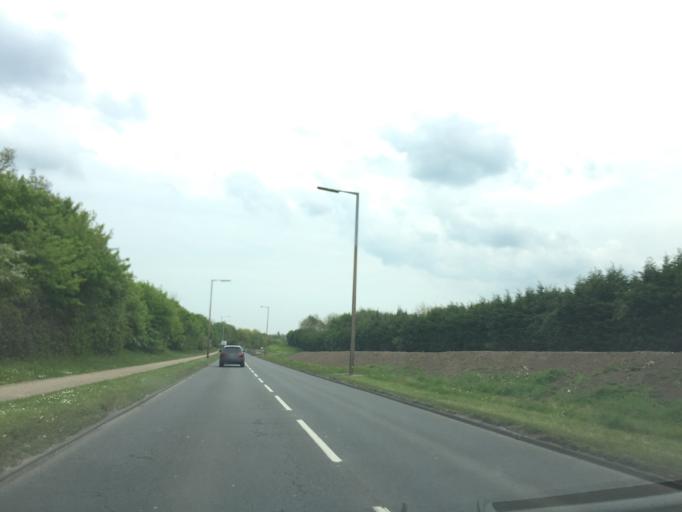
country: GB
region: England
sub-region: Essex
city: Roydon
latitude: 51.7628
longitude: 0.0714
